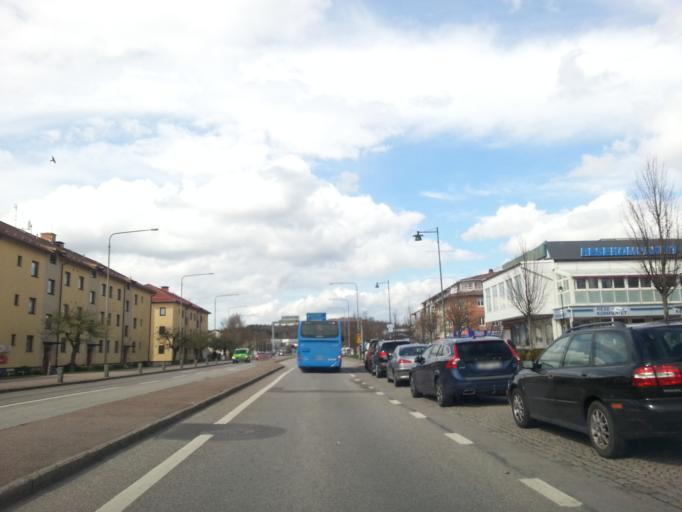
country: SE
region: Vaestra Goetaland
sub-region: Kungalvs Kommun
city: Kungalv
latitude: 57.8729
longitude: 11.9784
